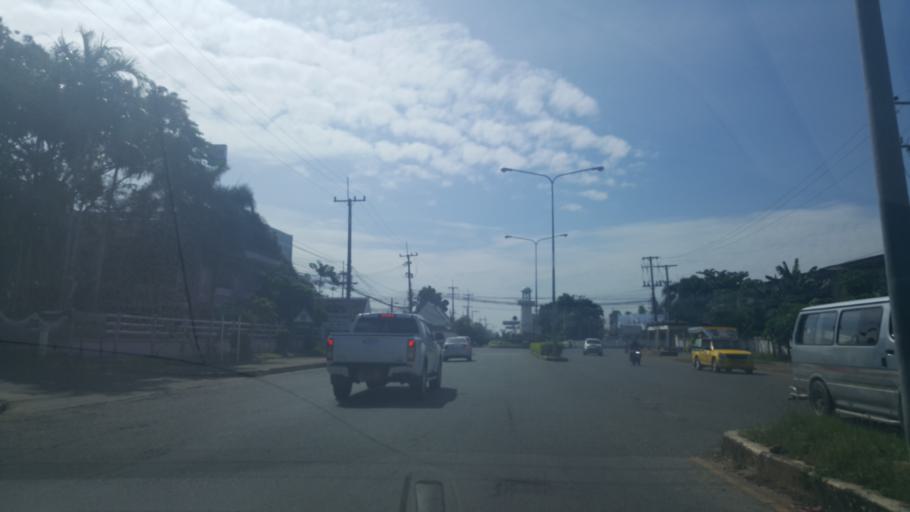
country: TH
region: Chon Buri
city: Sattahip
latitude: 12.6658
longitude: 100.8965
